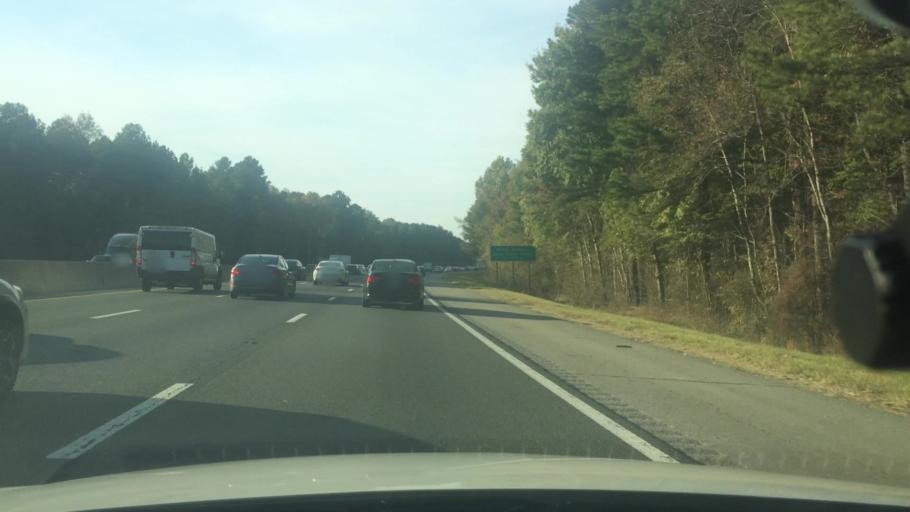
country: US
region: North Carolina
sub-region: Orange County
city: Chapel Hill
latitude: 35.9067
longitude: -78.9748
